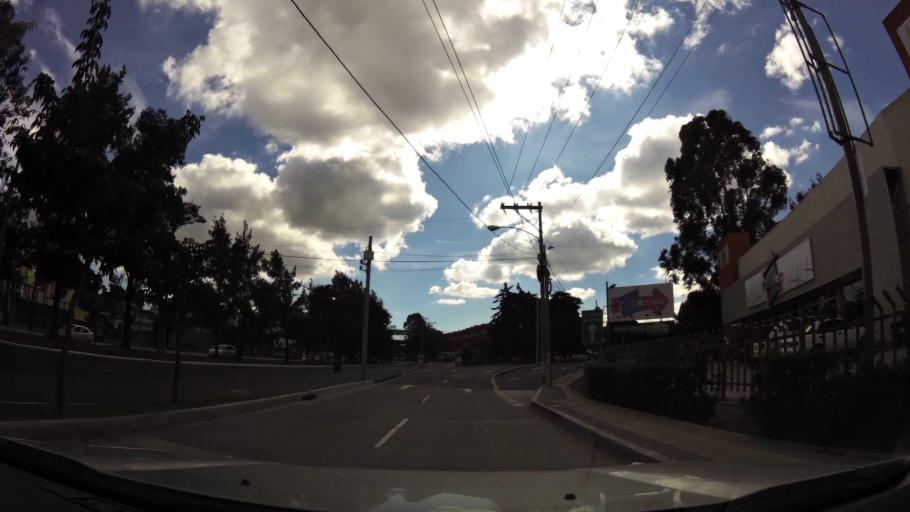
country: GT
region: Guatemala
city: Mixco
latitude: 14.6035
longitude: -90.5612
